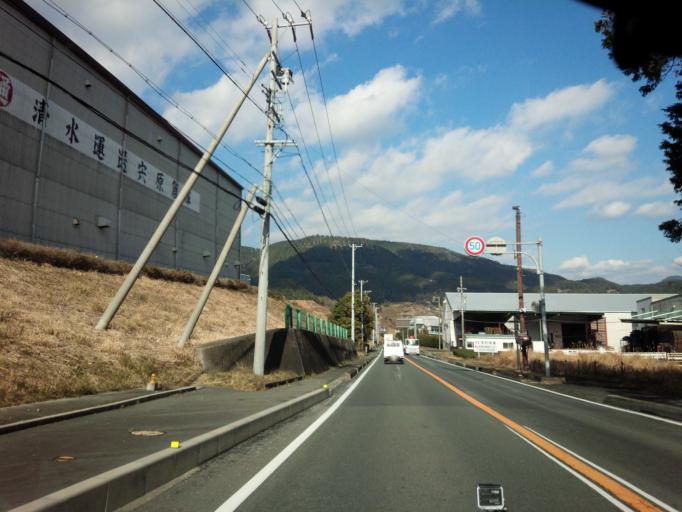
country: JP
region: Shizuoka
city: Fujinomiya
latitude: 35.1543
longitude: 138.5204
